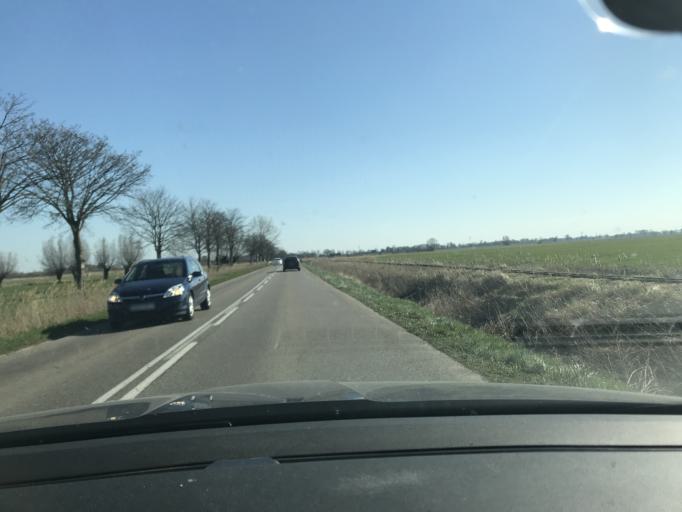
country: PL
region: Pomeranian Voivodeship
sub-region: Powiat nowodworski
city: Nowy Dwor Gdanski
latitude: 54.2552
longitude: 19.1387
